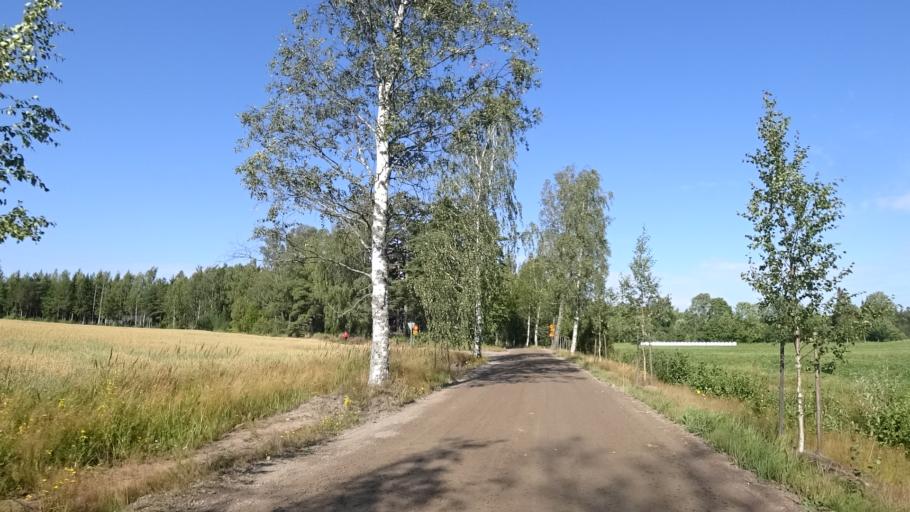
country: FI
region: Kymenlaakso
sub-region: Kotka-Hamina
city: Hamina
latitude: 60.5386
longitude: 27.2238
